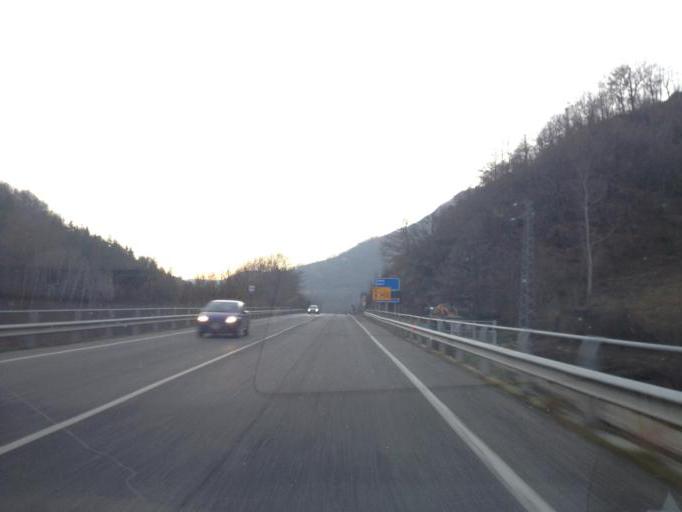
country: IT
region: The Marches
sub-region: Provincia di Ascoli Piceno
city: Arquata del Tronto
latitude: 42.7691
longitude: 13.2933
